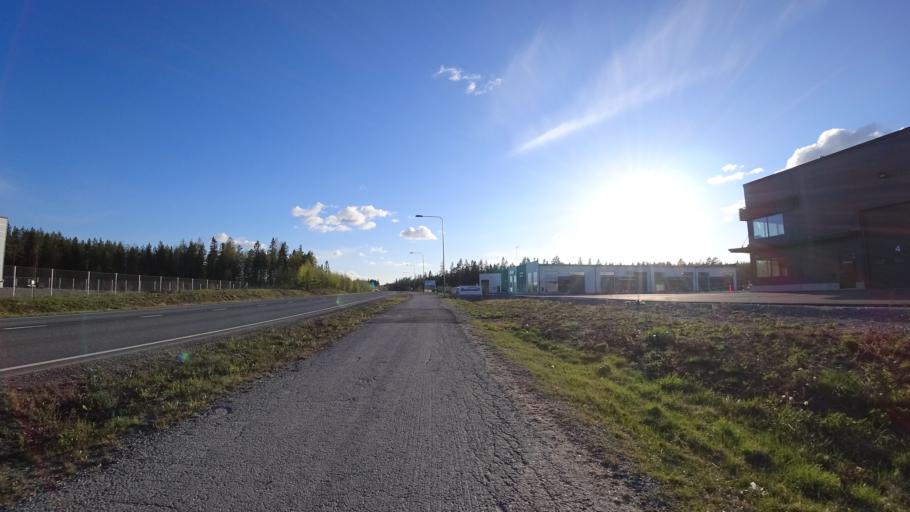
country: FI
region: Pirkanmaa
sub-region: Tampere
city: Yloejaervi
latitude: 61.4988
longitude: 23.5612
